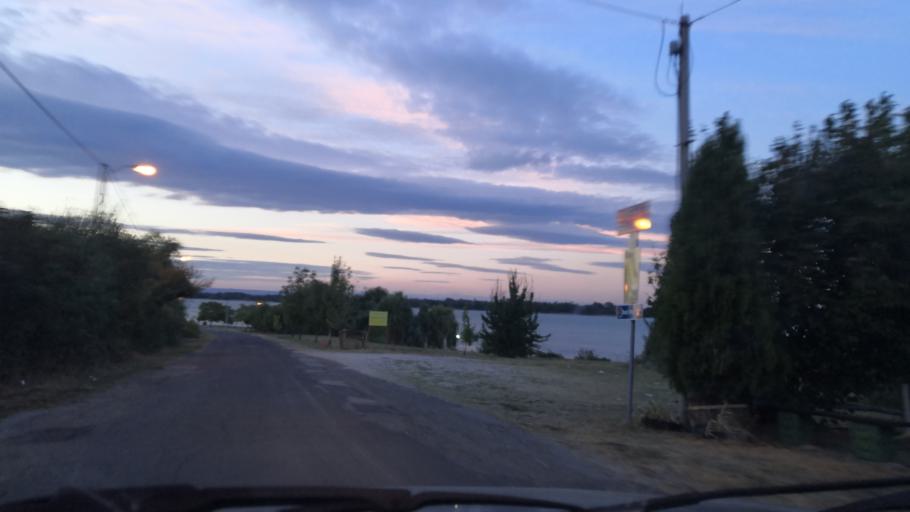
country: RO
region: Mehedinti
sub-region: Comuna Gogosu
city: Balta Verde
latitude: 44.3141
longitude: 22.5481
